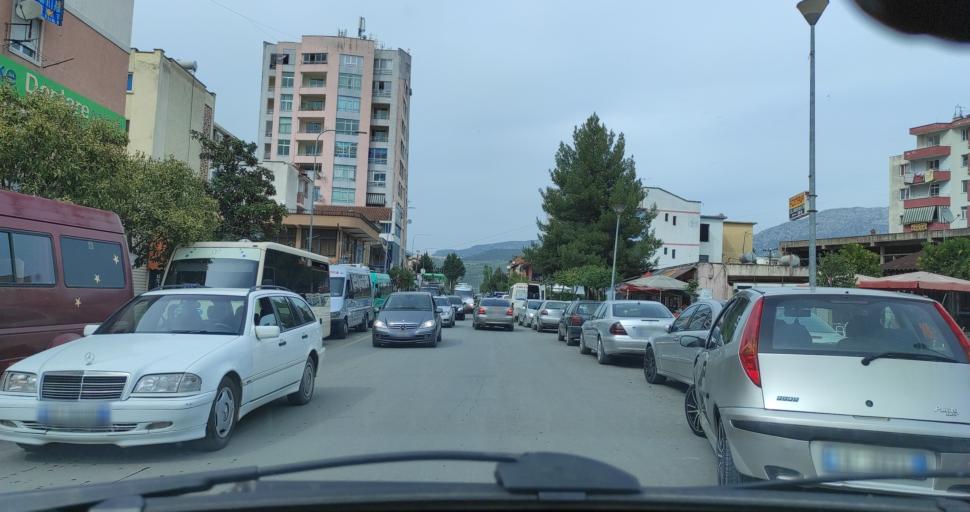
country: AL
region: Durres
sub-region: Rrethi i Krujes
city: Fushe-Kruje
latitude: 41.4793
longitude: 19.7208
